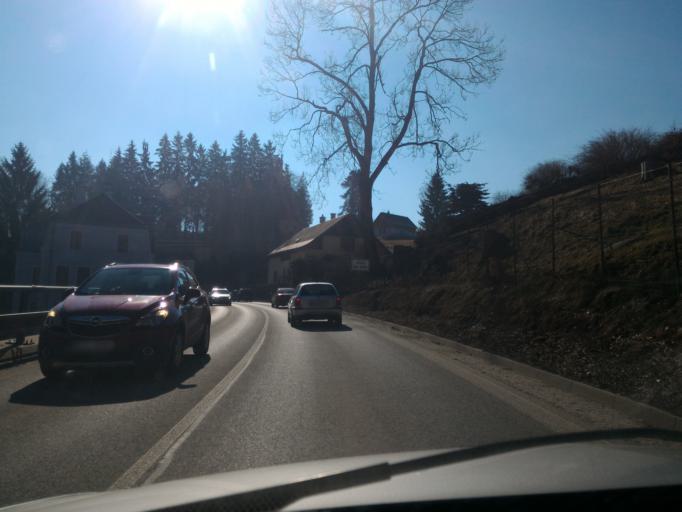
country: CZ
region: Liberecky
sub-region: Okres Jablonec nad Nisou
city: Lucany nad Nisou
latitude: 50.7394
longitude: 15.2089
